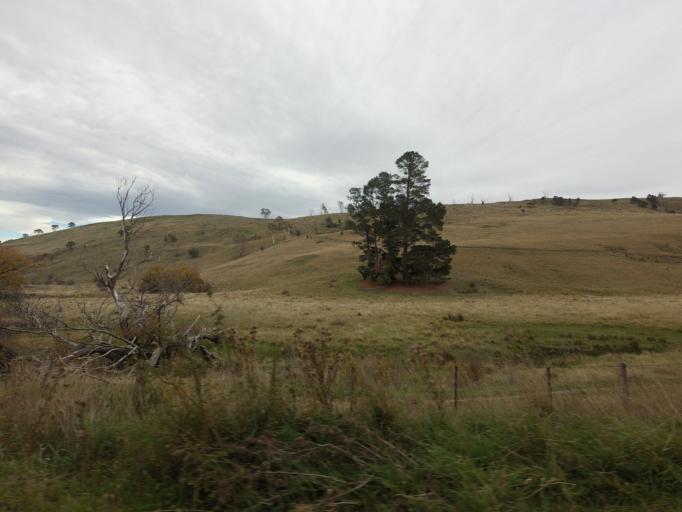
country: AU
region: Tasmania
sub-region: Derwent Valley
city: New Norfolk
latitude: -42.3664
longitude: 146.8424
